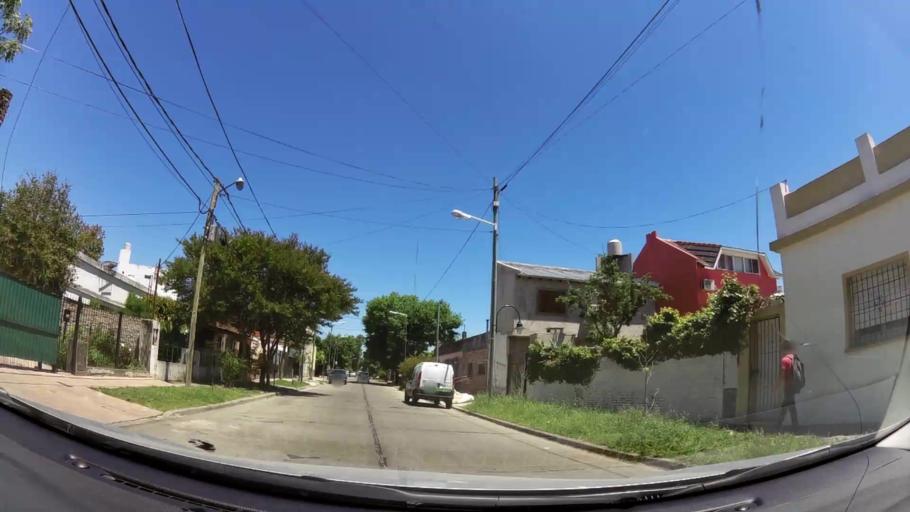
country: AR
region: Buenos Aires
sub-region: Partido de Tigre
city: Tigre
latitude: -34.4539
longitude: -58.5545
